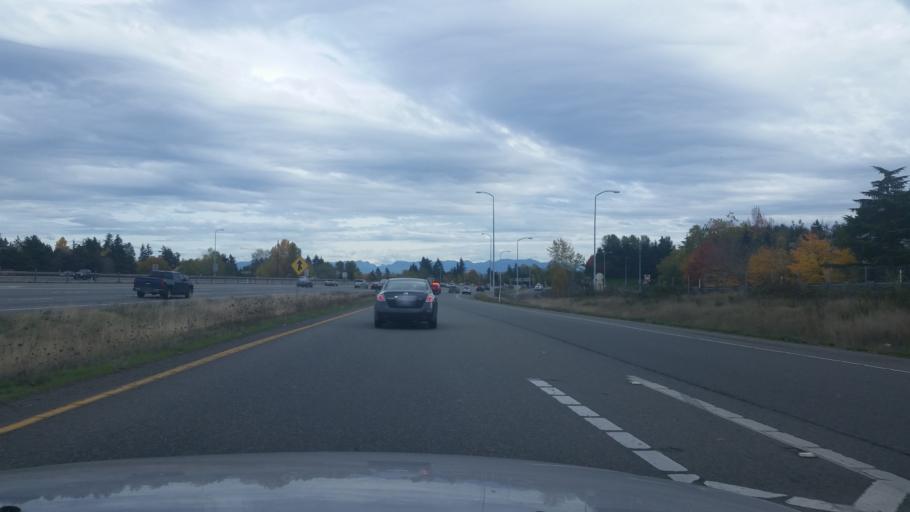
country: US
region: Washington
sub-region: King County
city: Eastgate
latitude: 47.5784
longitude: -122.1363
